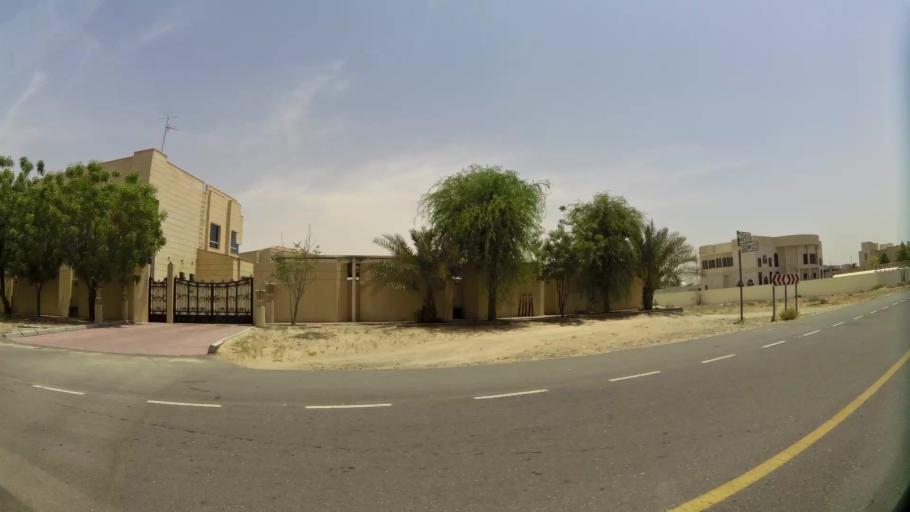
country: AE
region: Ash Shariqah
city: Sharjah
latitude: 25.2361
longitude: 55.4830
